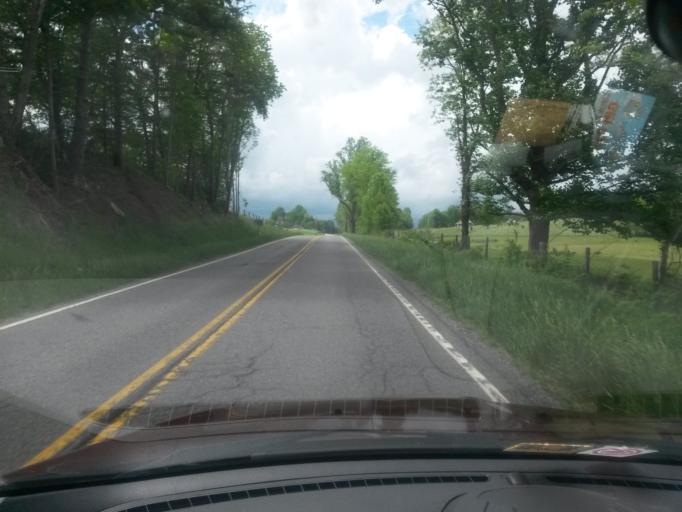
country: US
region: Virginia
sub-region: Floyd County
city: Floyd
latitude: 36.8606
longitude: -80.3241
